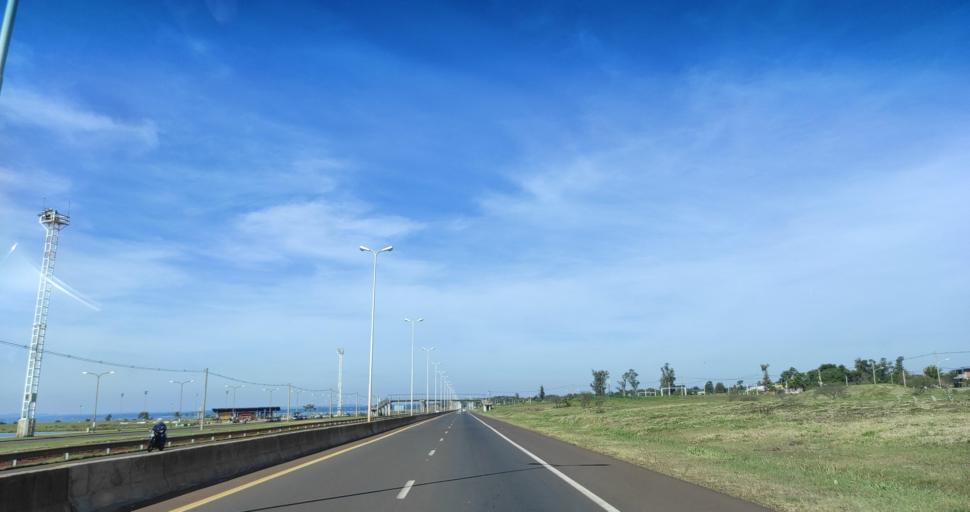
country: AR
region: Misiones
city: Garupa
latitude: -27.4304
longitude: -55.8678
